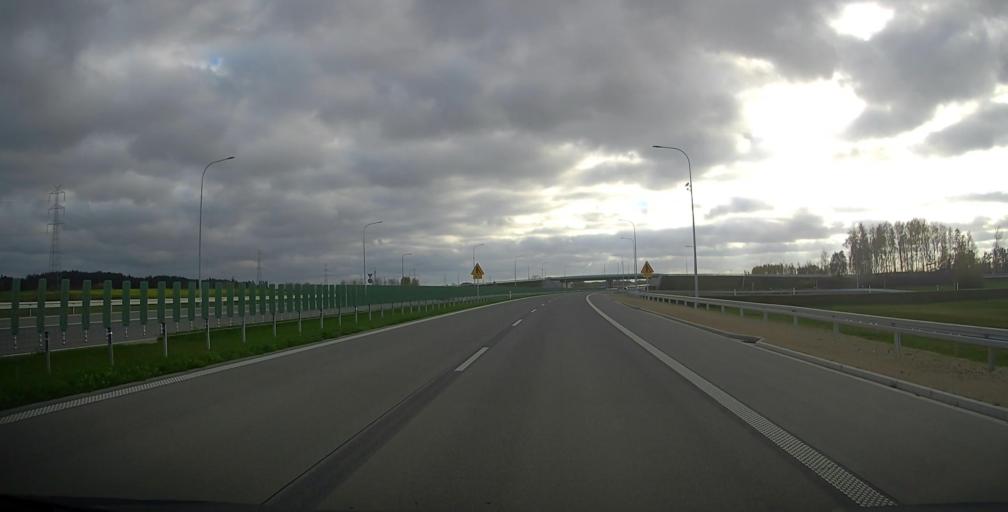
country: PL
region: Podlasie
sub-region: Powiat grajewski
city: Szczuczyn
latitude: 53.5926
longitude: 22.3276
